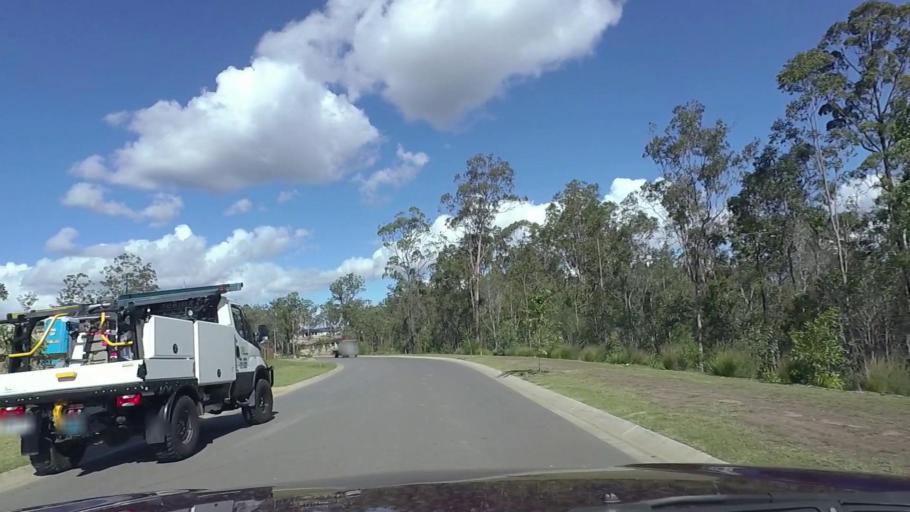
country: AU
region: Queensland
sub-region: Ipswich
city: Springfield Lakes
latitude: -27.7485
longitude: 152.9203
